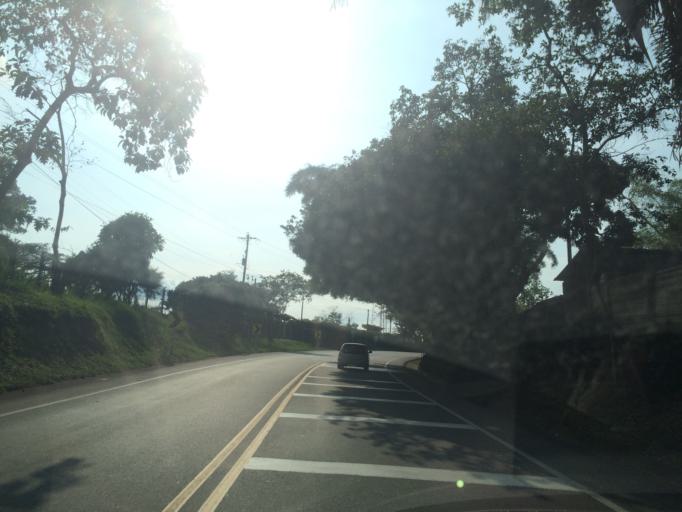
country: CO
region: Quindio
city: La Tebaida
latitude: 4.4449
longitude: -75.8333
